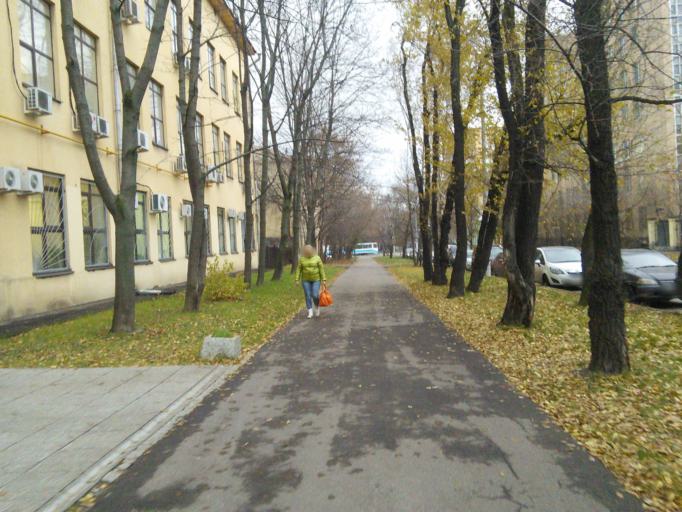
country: RU
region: Moskovskaya
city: Leninskiye Gory
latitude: 55.6982
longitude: 37.5694
